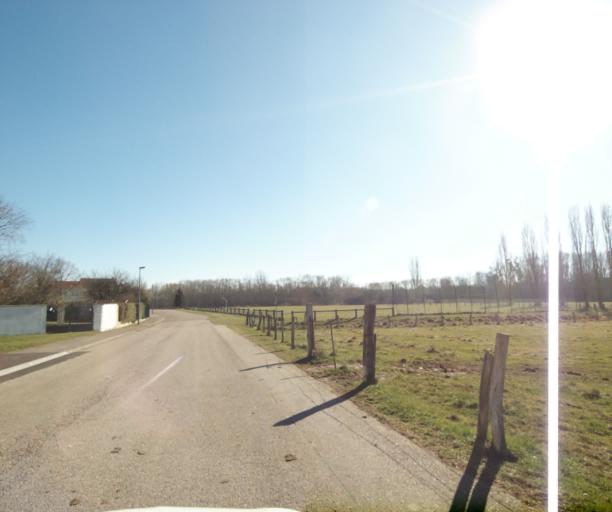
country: FR
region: Lorraine
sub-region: Departement de Meurthe-et-Moselle
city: Tomblaine
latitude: 48.6771
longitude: 6.2149
